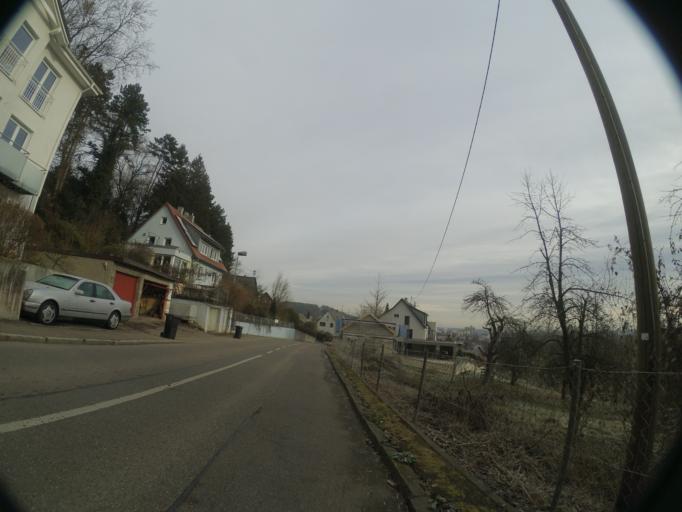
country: DE
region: Bavaria
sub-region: Swabia
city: Neu-Ulm
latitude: 48.4327
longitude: 10.0422
